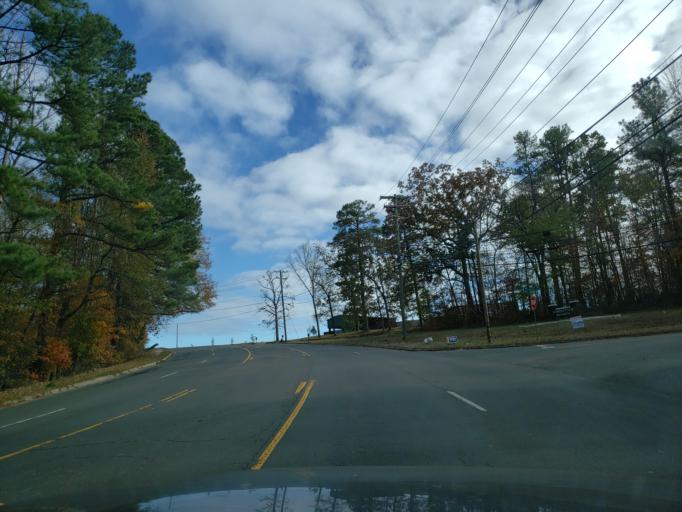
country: US
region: North Carolina
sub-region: Durham County
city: Durham
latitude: 35.9612
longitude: -78.9150
